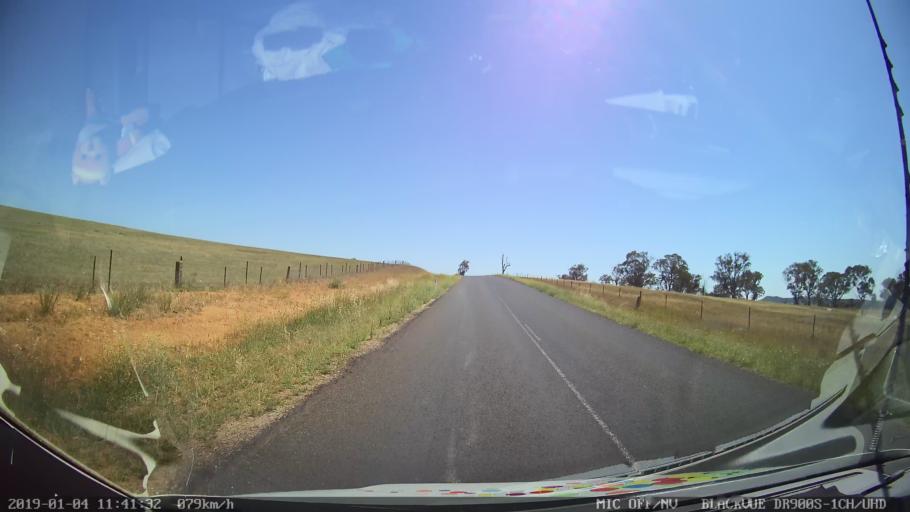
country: AU
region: New South Wales
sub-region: Cabonne
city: Molong
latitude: -32.9926
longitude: 148.7878
